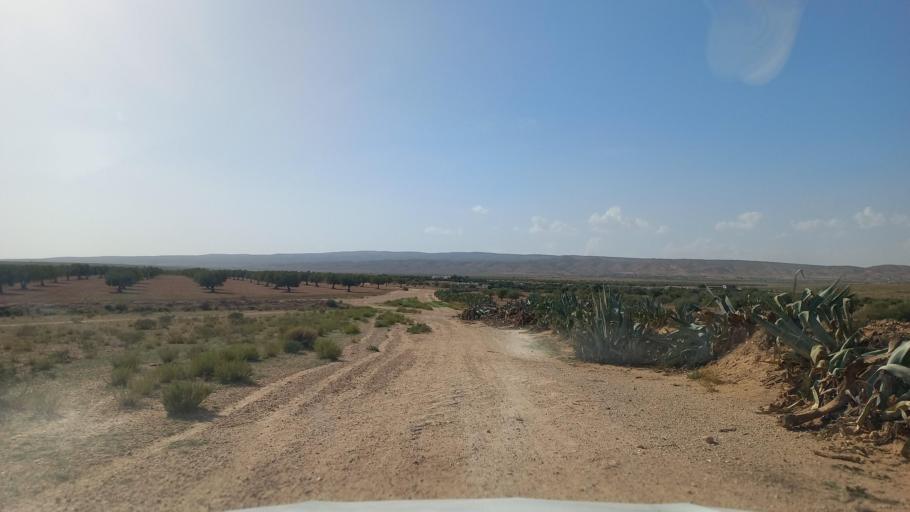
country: TN
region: Al Qasrayn
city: Kasserine
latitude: 35.3132
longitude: 9.0173
